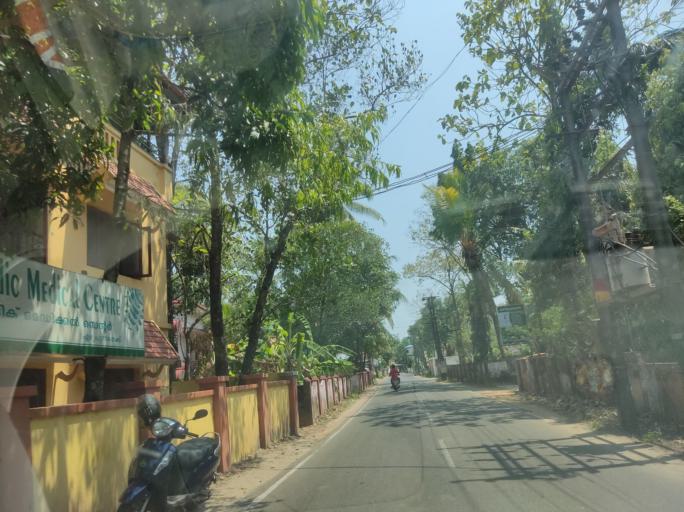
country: IN
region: Kerala
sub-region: Alappuzha
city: Kutiatodu
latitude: 9.7964
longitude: 76.3022
